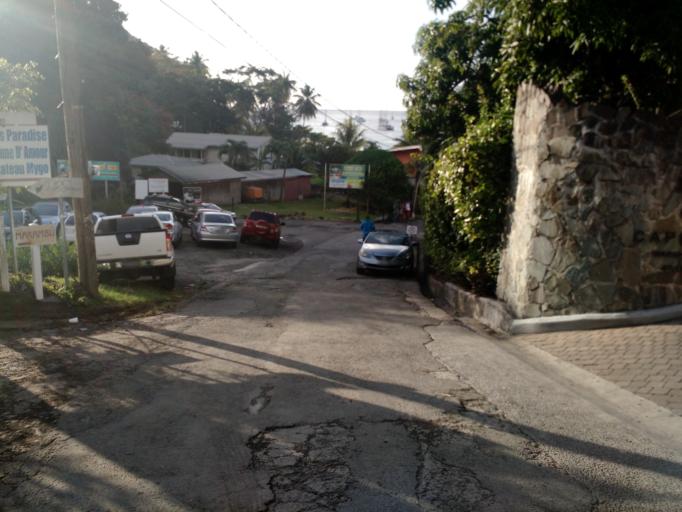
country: LC
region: Anse-la-Raye
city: Anse La Raye
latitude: 13.9644
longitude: -61.0240
